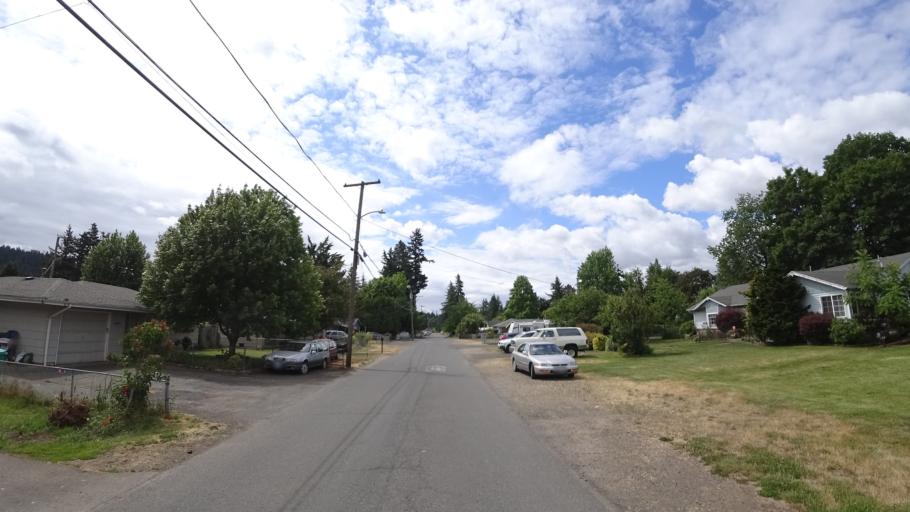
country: US
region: Oregon
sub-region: Multnomah County
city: Lents
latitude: 45.4943
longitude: -122.5275
